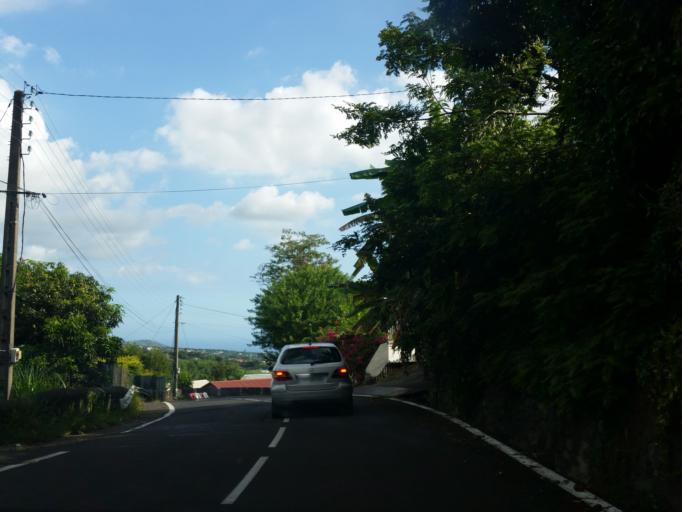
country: RE
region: Reunion
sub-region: Reunion
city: L'Entre-Deux
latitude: -21.2437
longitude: 55.4809
